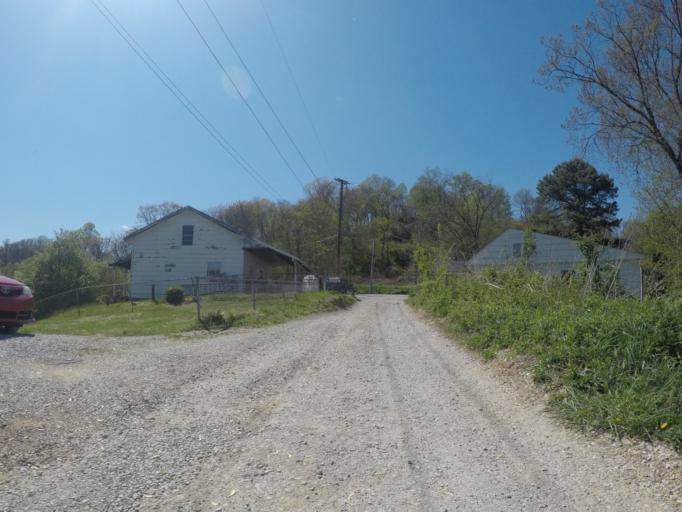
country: US
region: West Virginia
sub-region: Wayne County
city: Kenova
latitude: 38.3900
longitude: -82.5842
